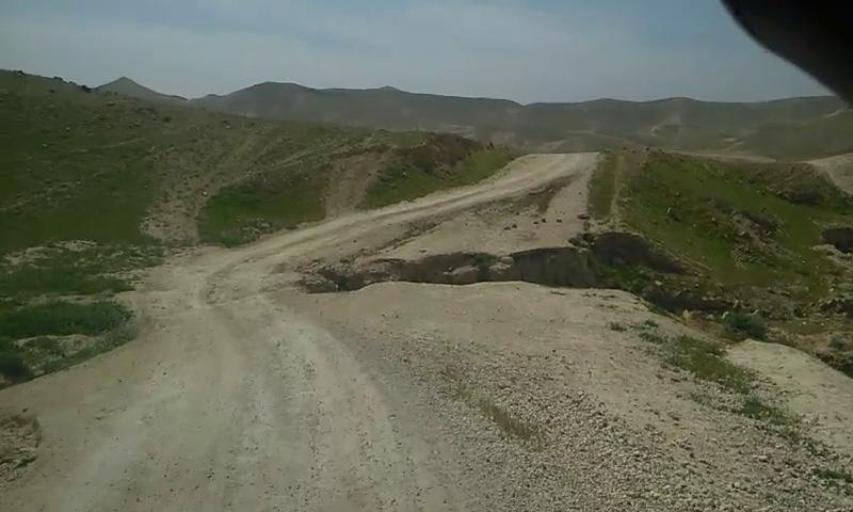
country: PS
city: `Arab ar Rashaydah
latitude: 31.5137
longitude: 35.2841
